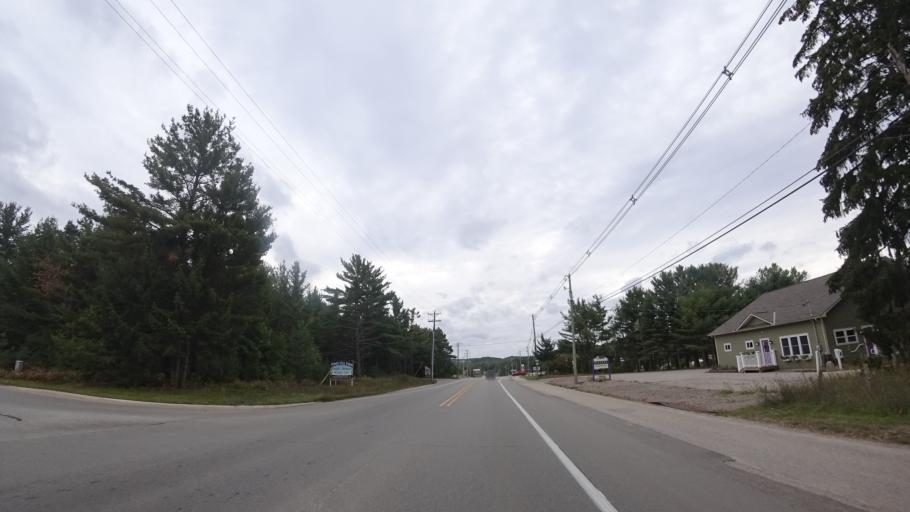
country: US
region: Michigan
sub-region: Emmet County
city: Petoskey
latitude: 45.4219
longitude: -84.9045
